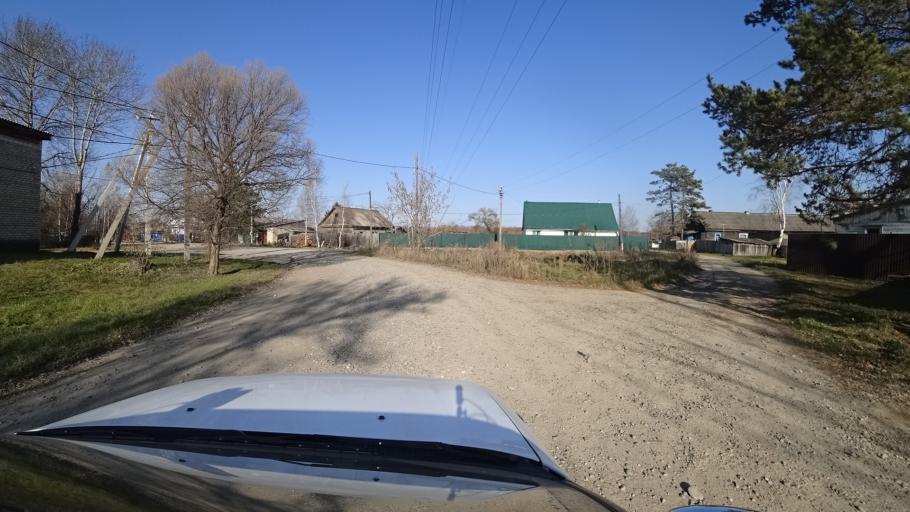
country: RU
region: Primorskiy
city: Dal'nerechensk
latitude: 45.9227
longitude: 133.7526
